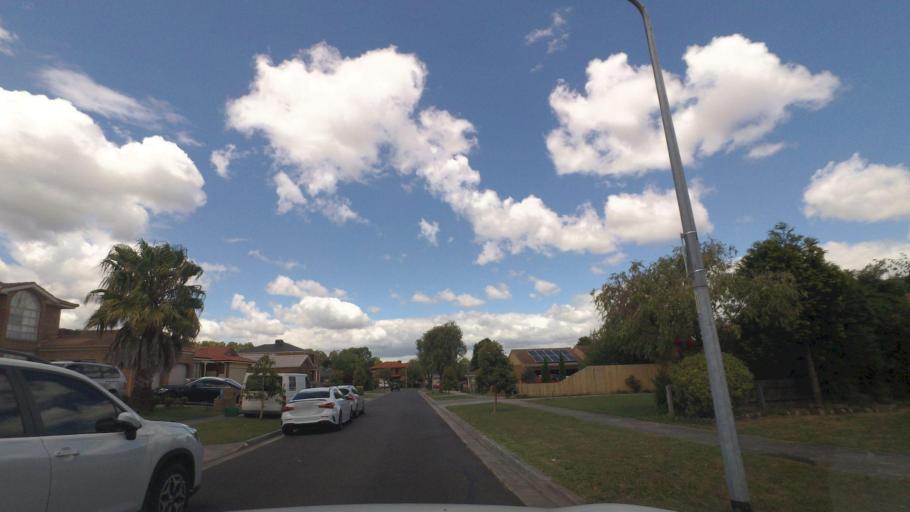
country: AU
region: Victoria
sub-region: Knox
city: Knoxfield
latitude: -37.9064
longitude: 145.2654
